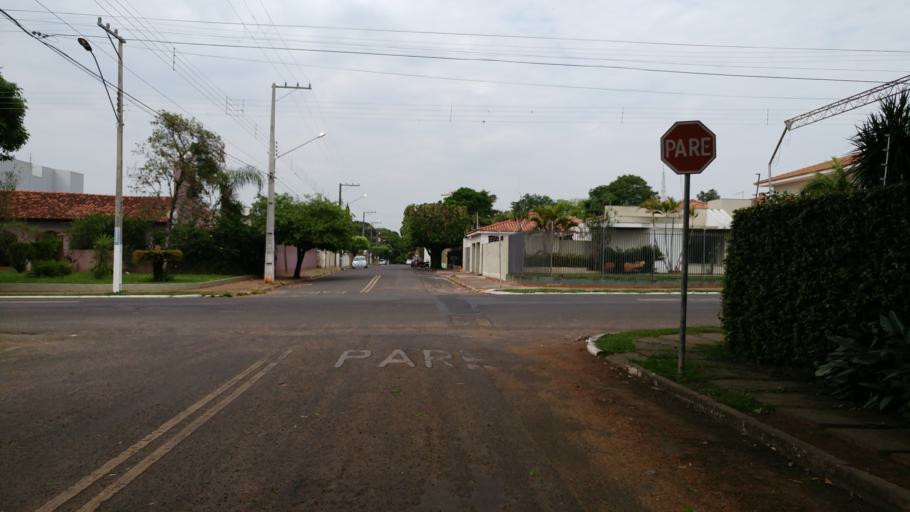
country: BR
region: Sao Paulo
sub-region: Paraguacu Paulista
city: Paraguacu Paulista
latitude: -22.4125
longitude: -50.5813
